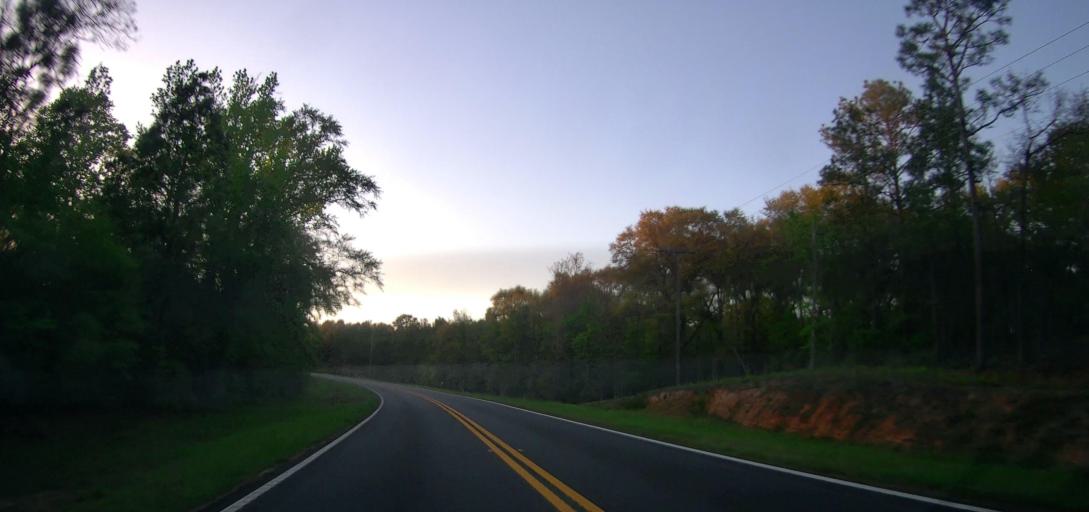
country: US
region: Georgia
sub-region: Marion County
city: Buena Vista
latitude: 32.4250
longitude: -84.5905
